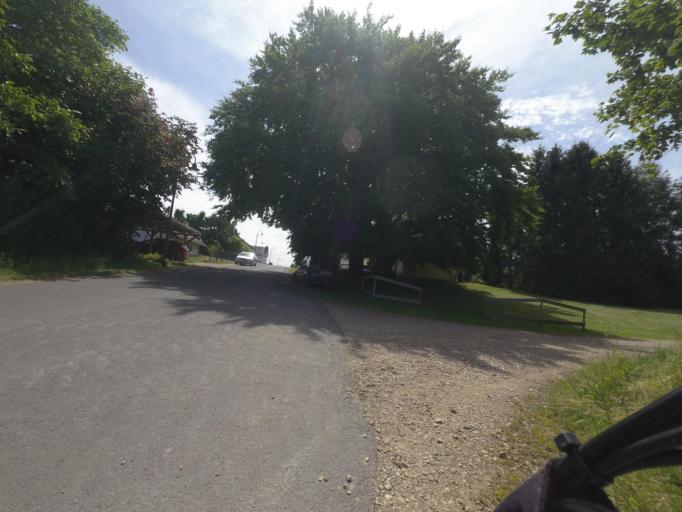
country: DE
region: Rheinland-Pfalz
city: Esch
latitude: 50.3690
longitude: 6.6040
